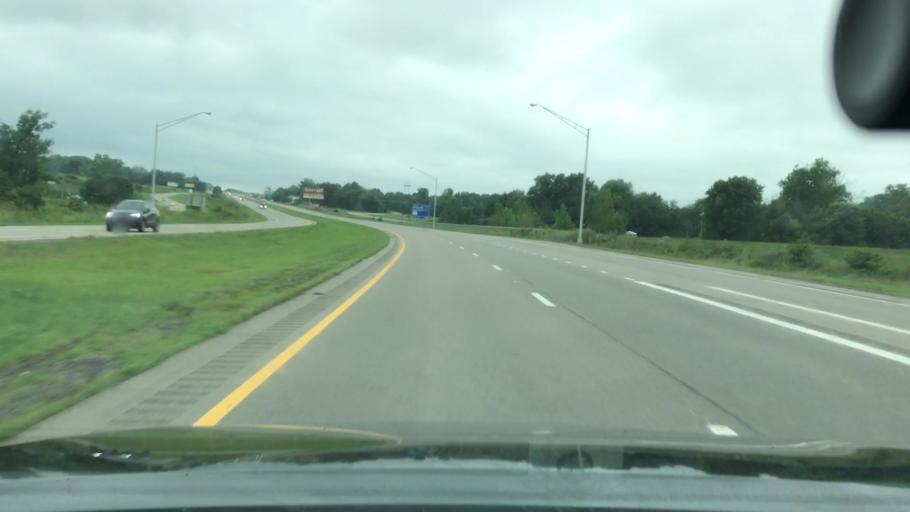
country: US
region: Ohio
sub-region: Ross County
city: Chillicothe
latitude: 39.4128
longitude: -82.9759
